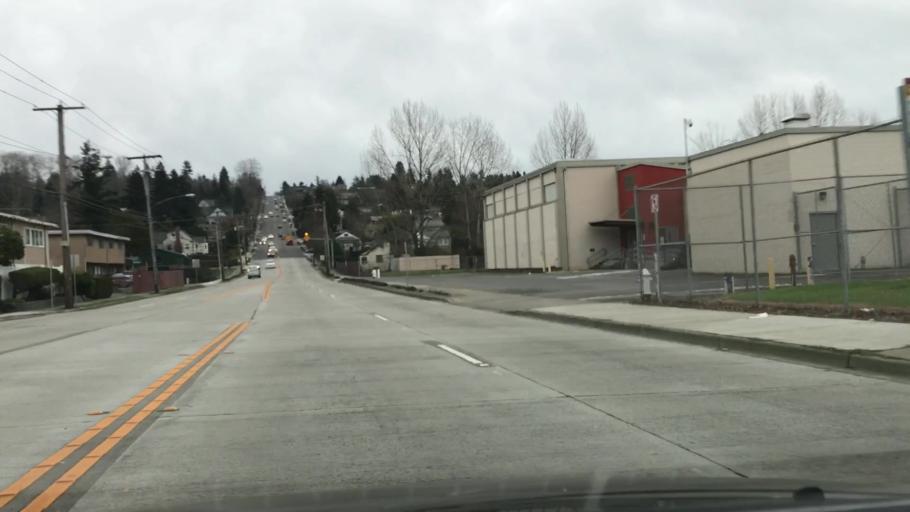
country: US
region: Washington
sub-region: King County
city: Kent
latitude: 47.3866
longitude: -122.2308
